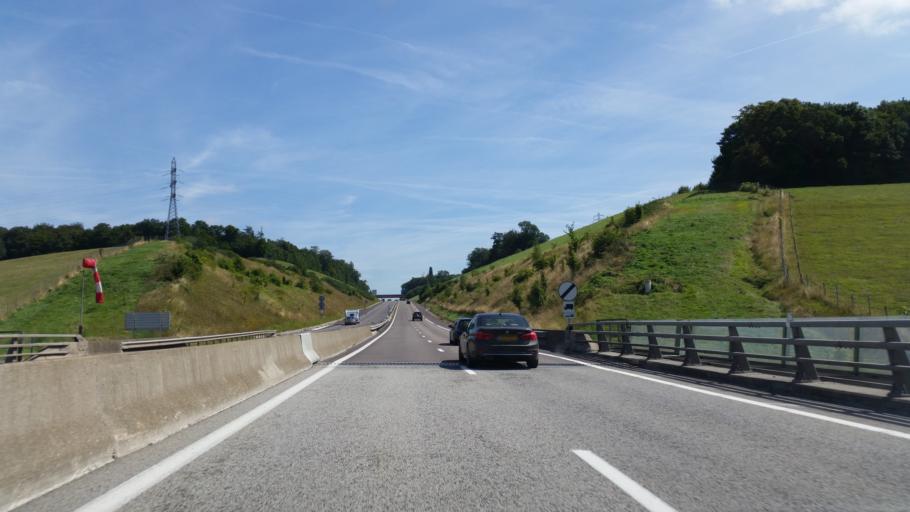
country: FR
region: Haute-Normandie
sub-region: Departement de la Seine-Maritime
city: Aumale
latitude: 49.7842
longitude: 1.7602
